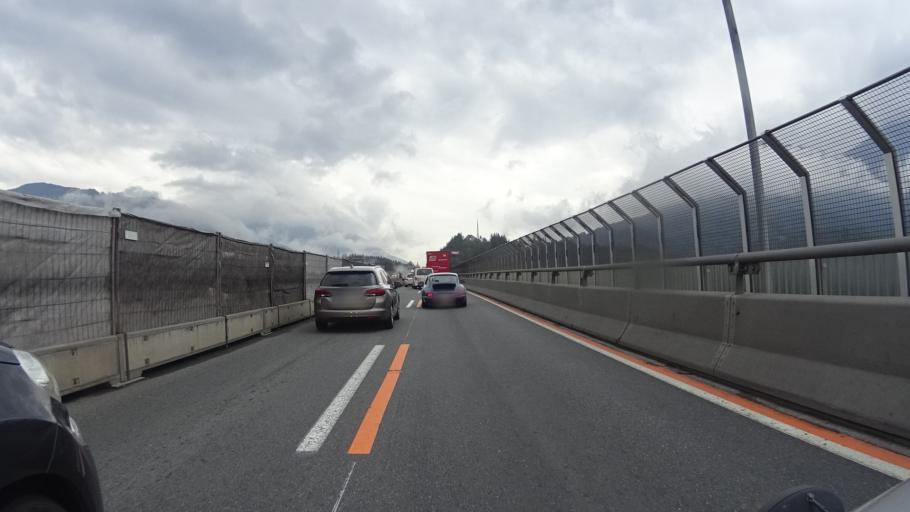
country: AT
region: Tyrol
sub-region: Politischer Bezirk Innsbruck Land
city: Patsch
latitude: 47.2034
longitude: 11.4039
